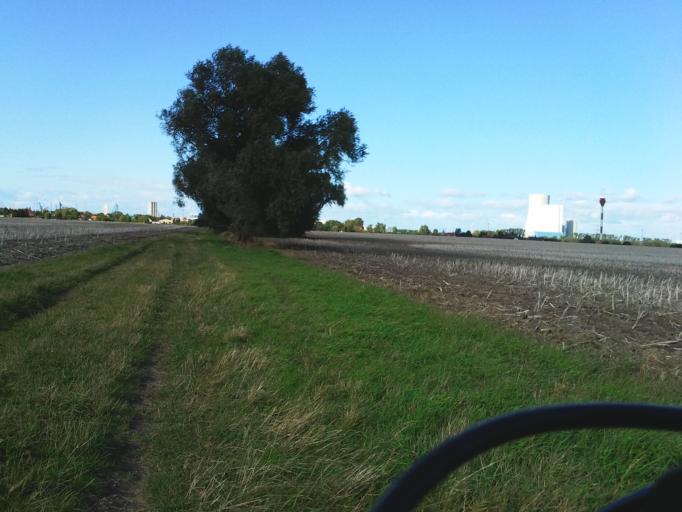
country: DE
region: Mecklenburg-Vorpommern
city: Dierkow-West
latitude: 54.1266
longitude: 12.1153
